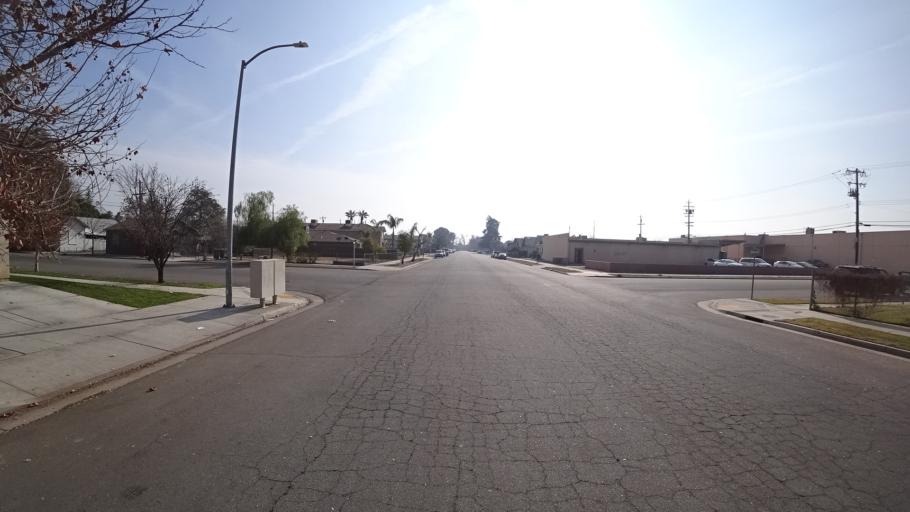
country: US
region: California
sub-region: Kern County
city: Bakersfield
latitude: 35.3639
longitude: -119.0177
